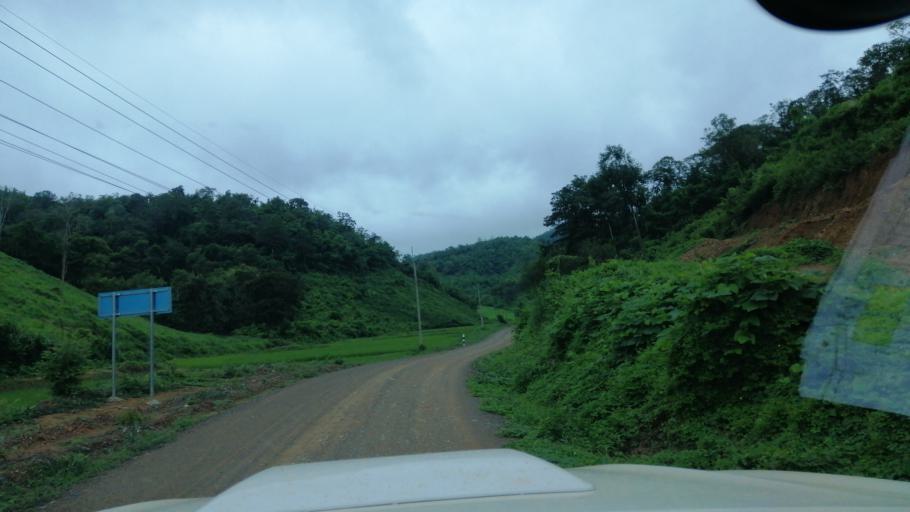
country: LA
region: Xiagnabouli
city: Muang Kenthao
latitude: 17.9426
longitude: 101.3997
